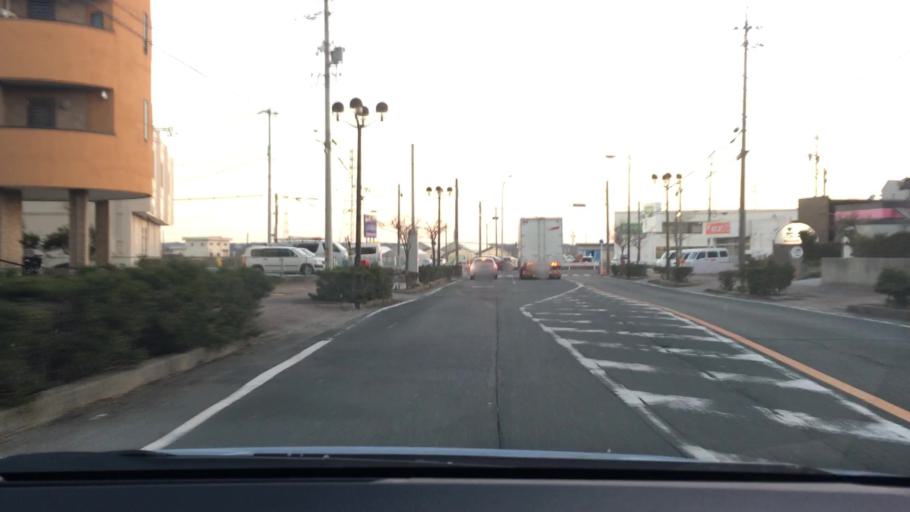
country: JP
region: Aichi
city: Tahara
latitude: 34.6614
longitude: 137.2669
